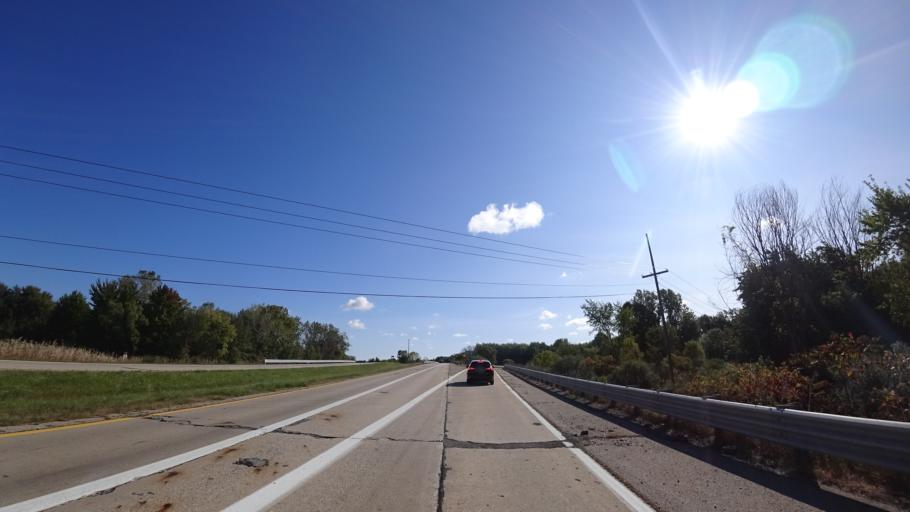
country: US
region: Michigan
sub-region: Berrien County
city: Benton Heights
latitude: 42.1191
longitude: -86.3947
